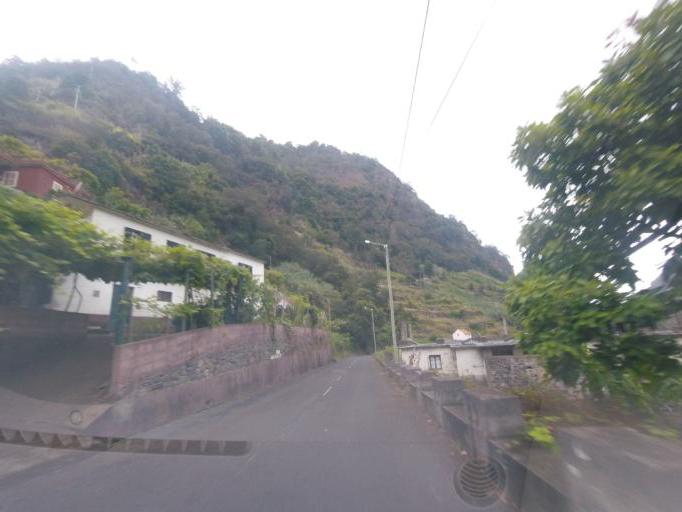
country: PT
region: Madeira
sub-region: Santana
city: Santana
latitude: 32.8184
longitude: -16.9002
